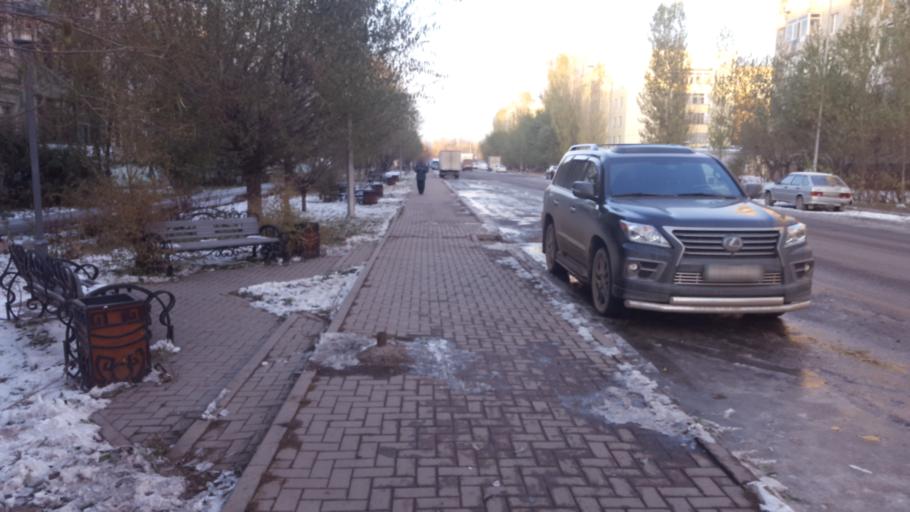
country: KZ
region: Astana Qalasy
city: Astana
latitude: 51.1571
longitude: 71.4906
